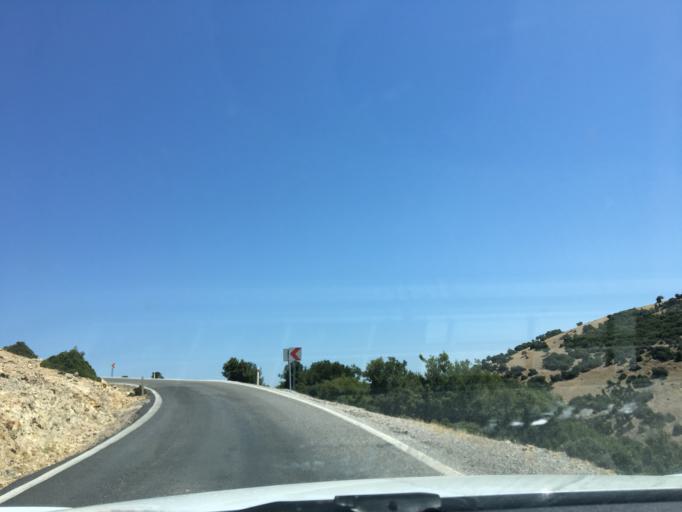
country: TR
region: Canakkale
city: Gulpinar
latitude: 39.4918
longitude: 26.1517
